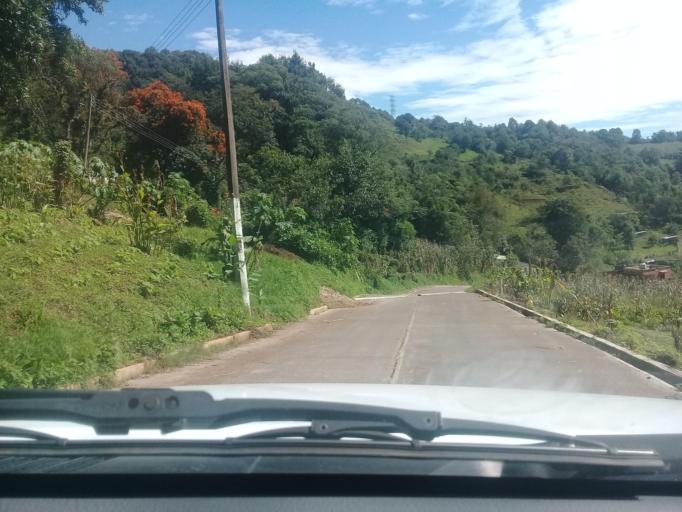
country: MX
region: Veracruz
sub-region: Tlalnelhuayocan
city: Otilpan
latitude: 19.5668
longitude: -96.9892
